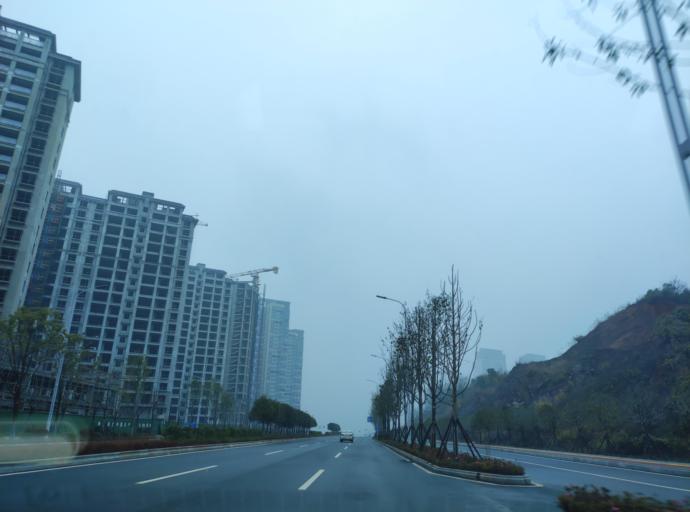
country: CN
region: Jiangxi Sheng
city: Pingxiang
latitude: 27.6655
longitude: 113.8431
